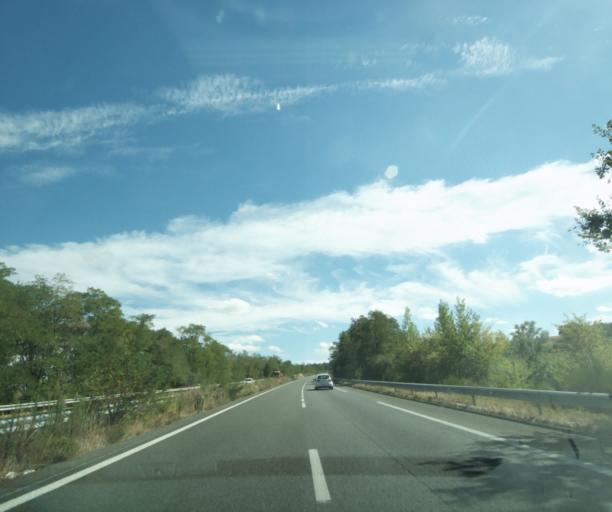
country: FR
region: Midi-Pyrenees
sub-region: Departement du Tarn-et-Garonne
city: Lamagistere
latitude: 44.0898
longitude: 0.7914
